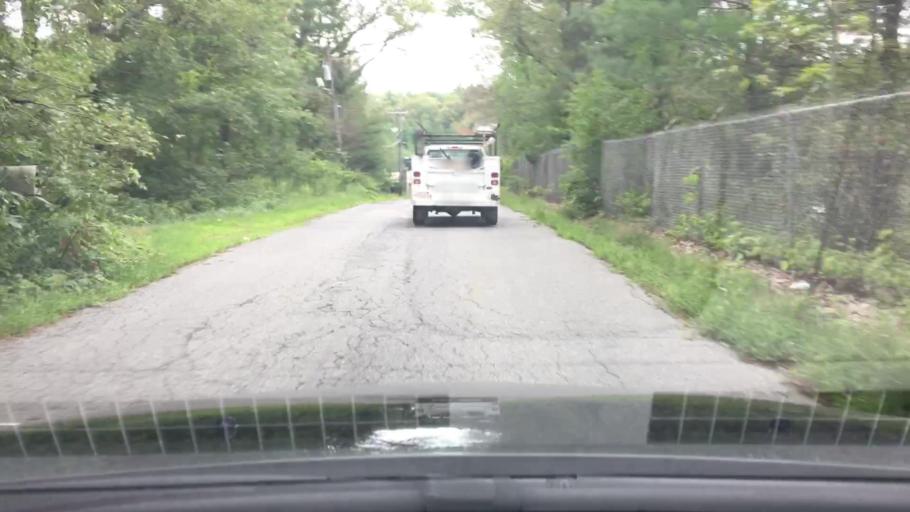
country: US
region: Massachusetts
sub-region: Worcester County
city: Northborough
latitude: 42.2846
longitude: -71.6603
